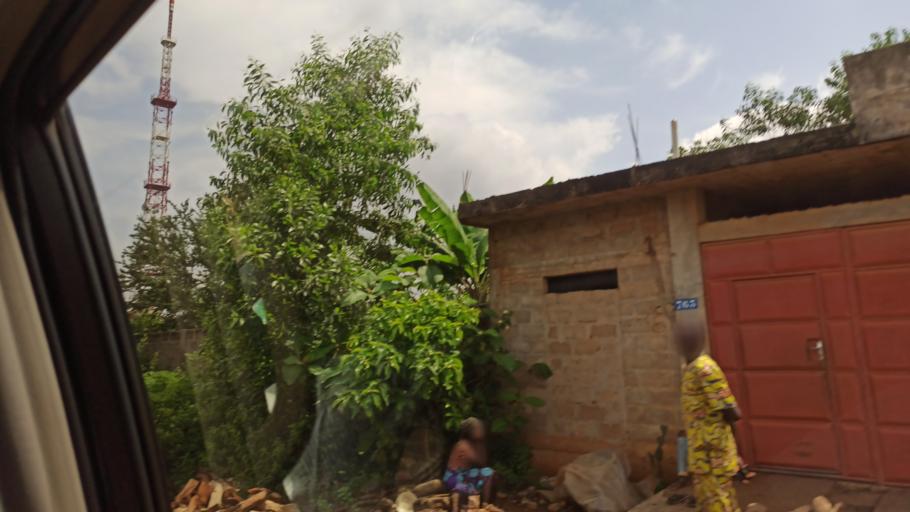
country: BJ
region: Queme
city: Porto-Novo
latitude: 6.4884
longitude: 2.5888
